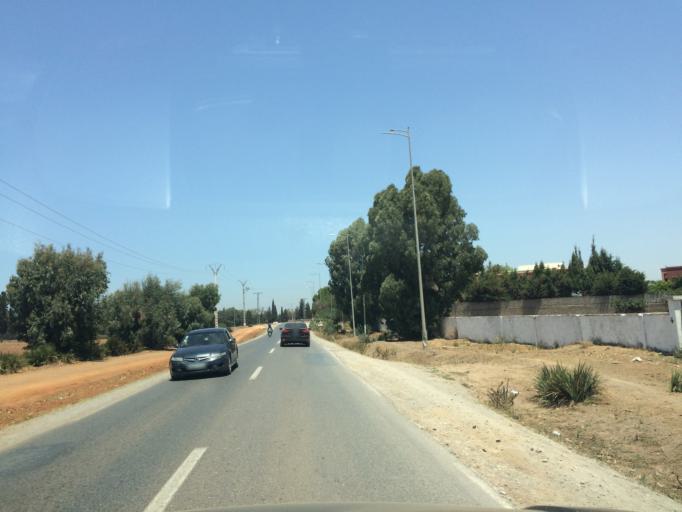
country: MA
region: Rabat-Sale-Zemmour-Zaer
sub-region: Skhirate-Temara
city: Temara
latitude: 33.8802
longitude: -6.8450
